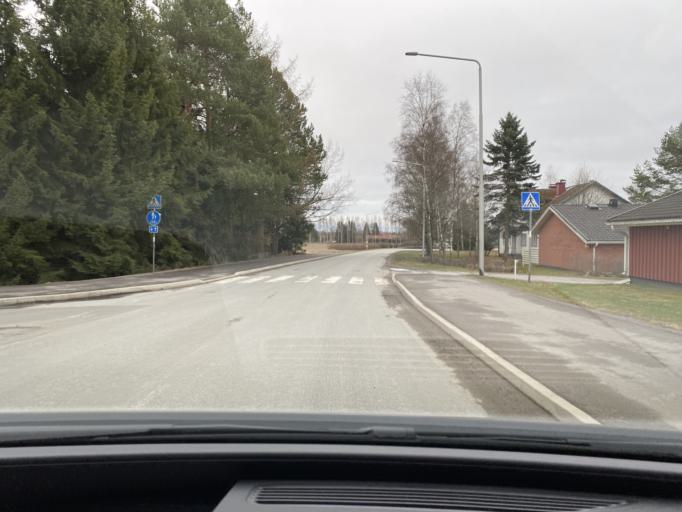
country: FI
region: Satakunta
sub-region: Pori
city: Huittinen
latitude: 61.1902
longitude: 22.7002
